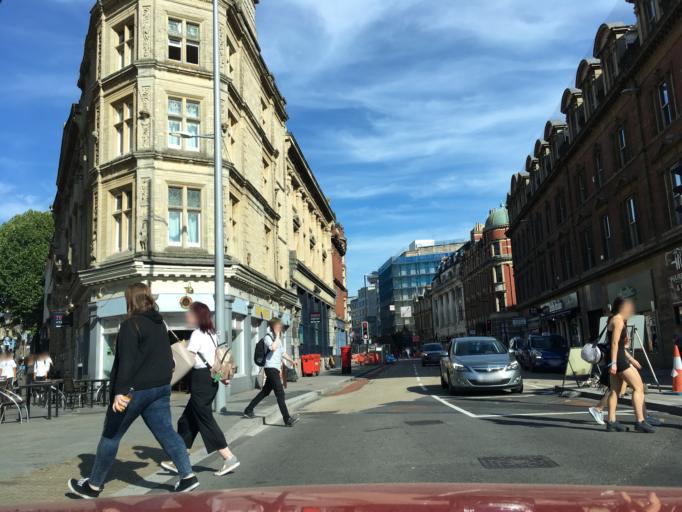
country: GB
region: England
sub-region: Bristol
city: Bristol
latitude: 51.4535
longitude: -2.5970
